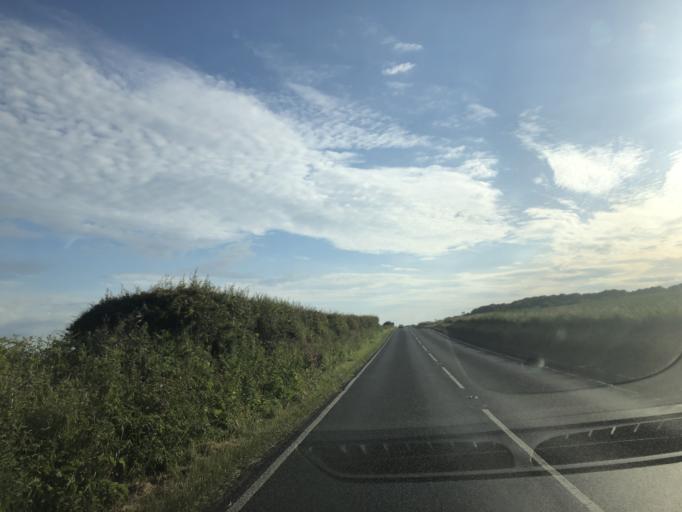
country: GB
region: Scotland
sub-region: Fife
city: Saint Monance
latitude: 56.1947
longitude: -2.7996
